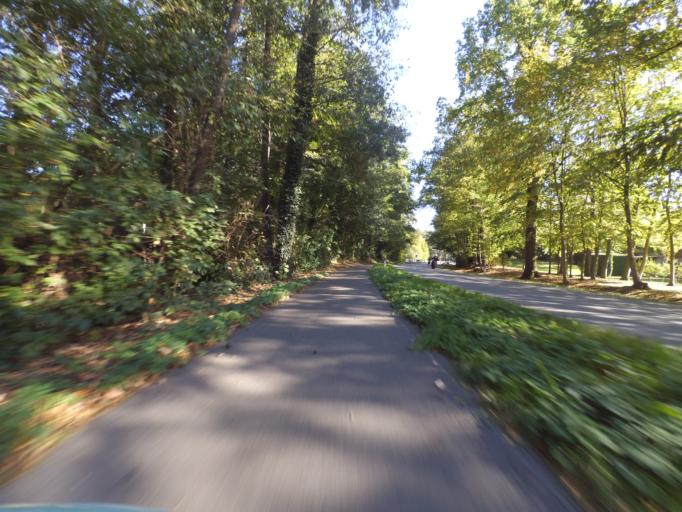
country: NL
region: Gelderland
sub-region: Gemeente Aalten
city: Bredevoort
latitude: 51.8898
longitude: 6.6544
